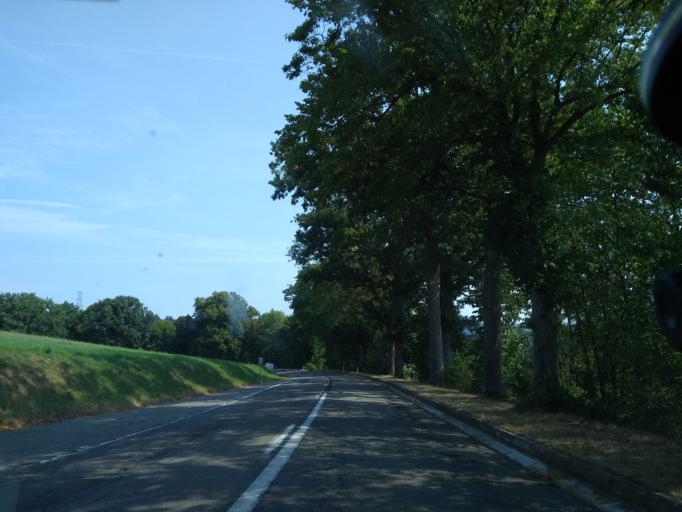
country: BE
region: Wallonia
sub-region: Province du Luxembourg
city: La Roche-en-Ardenne
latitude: 50.1649
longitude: 5.5621
